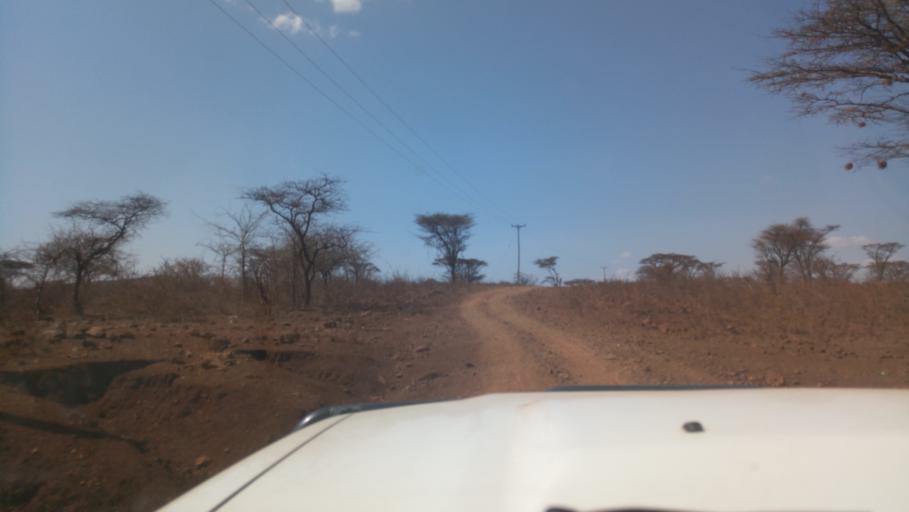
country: KE
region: Isiolo
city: Maua
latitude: 0.4228
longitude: 38.1870
